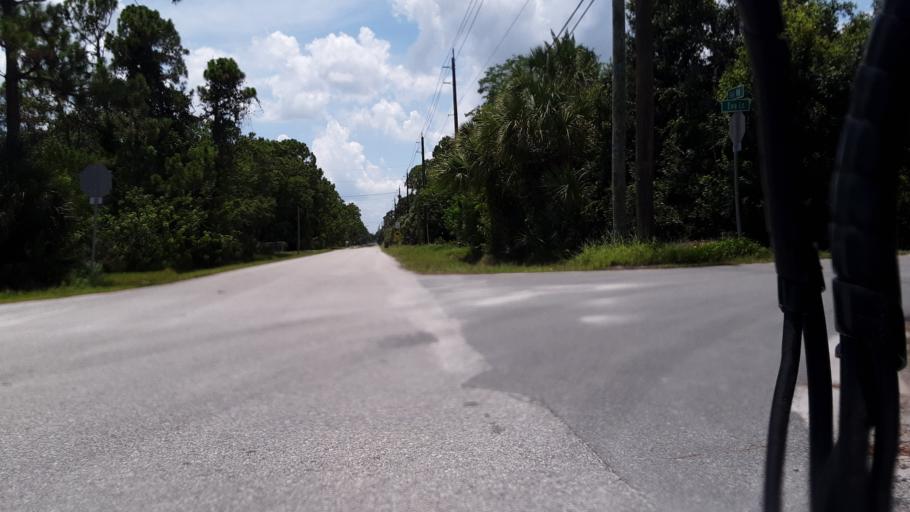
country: US
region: Florida
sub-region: Brevard County
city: Malabar
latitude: 27.9909
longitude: -80.5976
